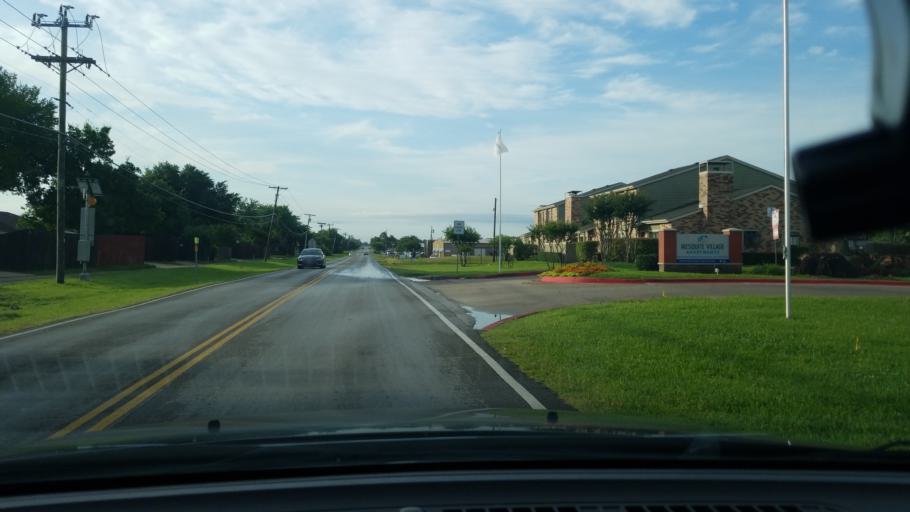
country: US
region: Texas
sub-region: Dallas County
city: Mesquite
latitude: 32.7996
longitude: -96.6210
